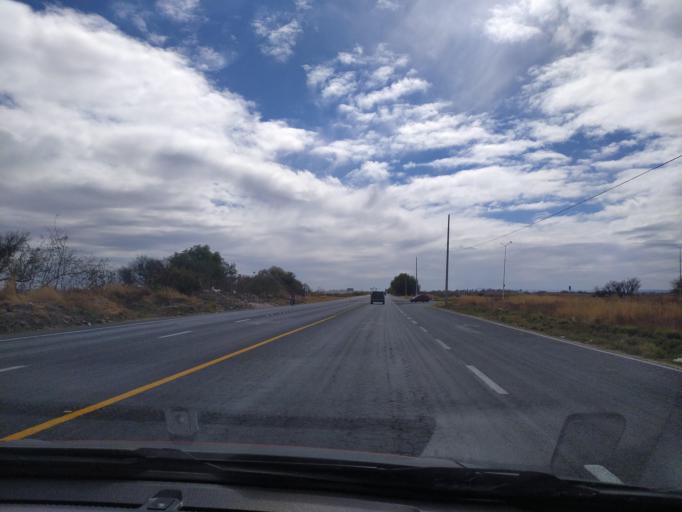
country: LA
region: Oudomxai
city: Muang La
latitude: 21.0125
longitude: 101.8284
